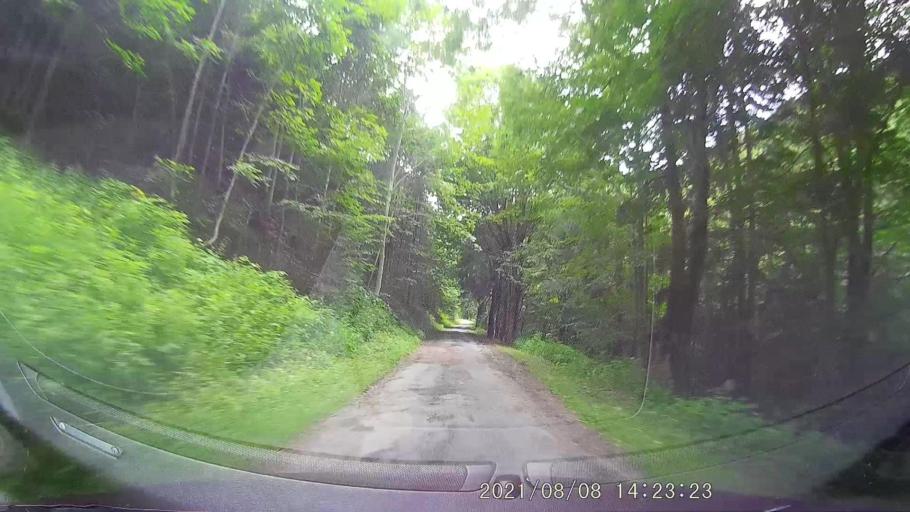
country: PL
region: Lower Silesian Voivodeship
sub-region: Powiat klodzki
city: Lewin Klodzki
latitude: 50.4411
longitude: 16.3043
